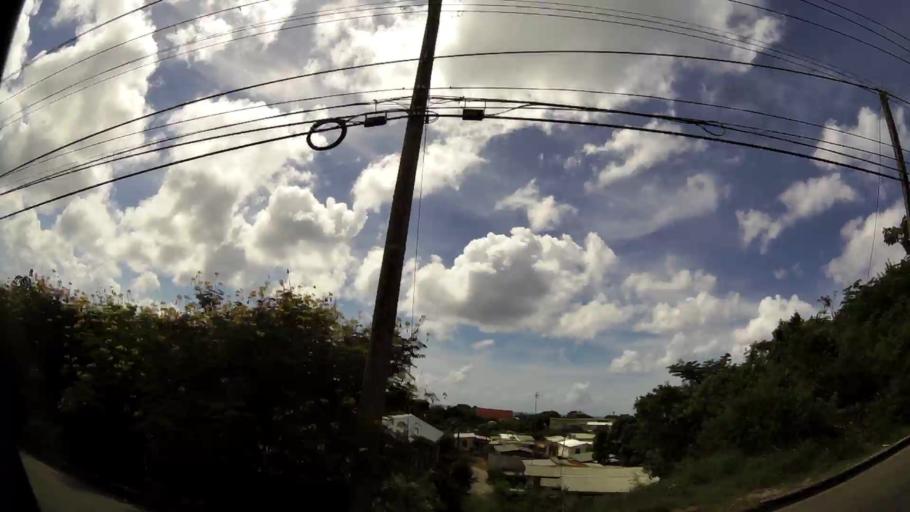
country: BB
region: Saint Michael
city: Bridgetown
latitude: 13.1303
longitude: -59.6236
